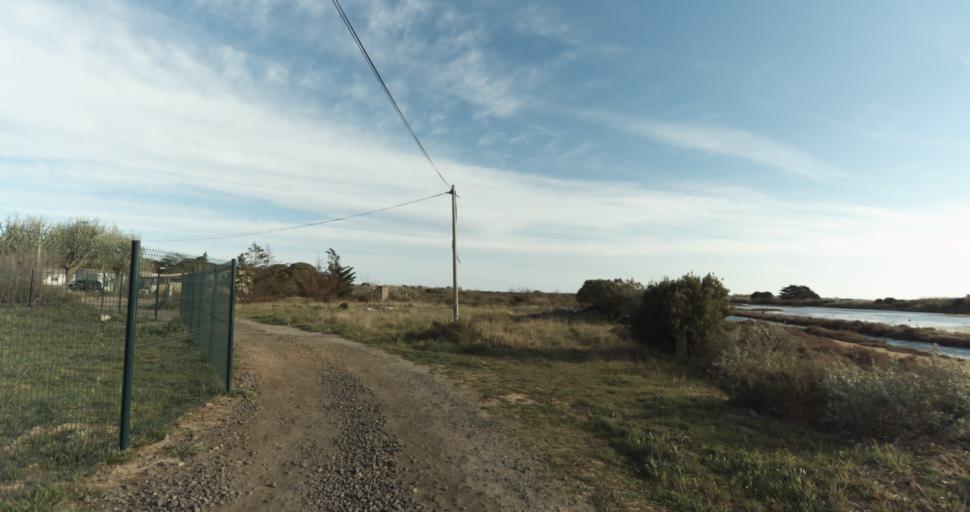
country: FR
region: Languedoc-Roussillon
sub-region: Departement de l'Herault
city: Le Cap d'Agde
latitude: 43.3139
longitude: 3.5315
